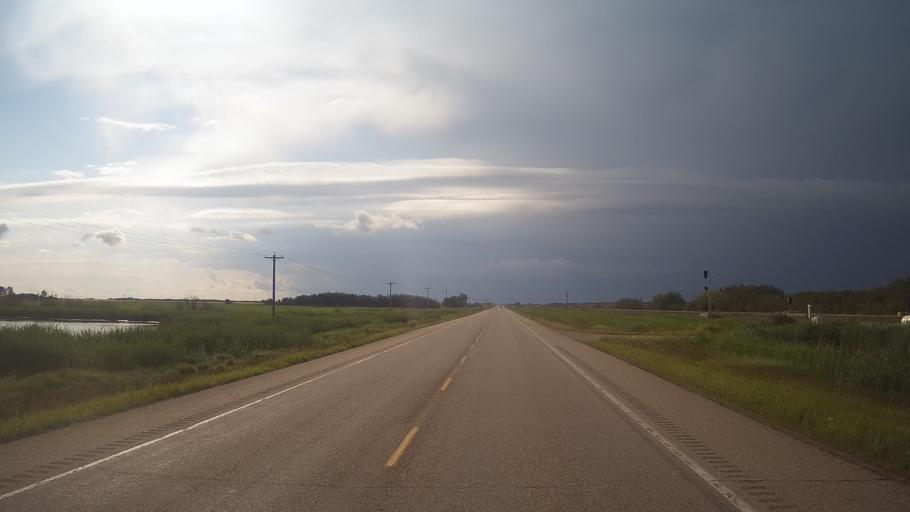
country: CA
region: Alberta
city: Vegreville
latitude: 53.1834
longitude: -112.0800
